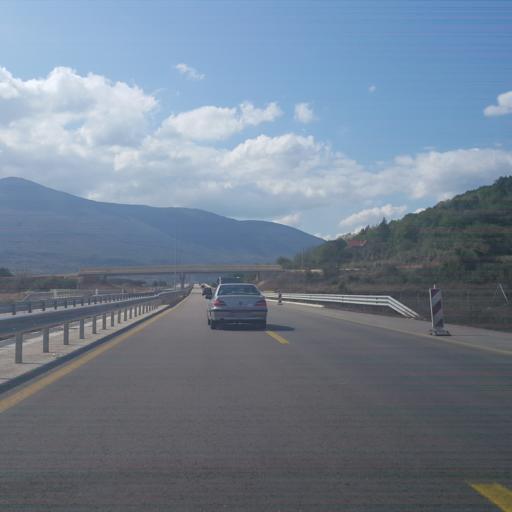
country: RS
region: Central Serbia
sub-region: Pirotski Okrug
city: Bela Palanka
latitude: 43.2377
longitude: 22.3313
